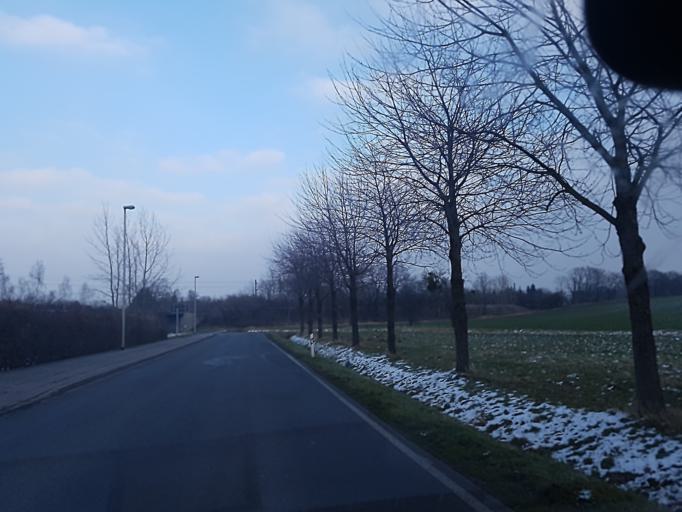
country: DE
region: Saxony
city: Oschatz
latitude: 51.3168
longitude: 13.0804
